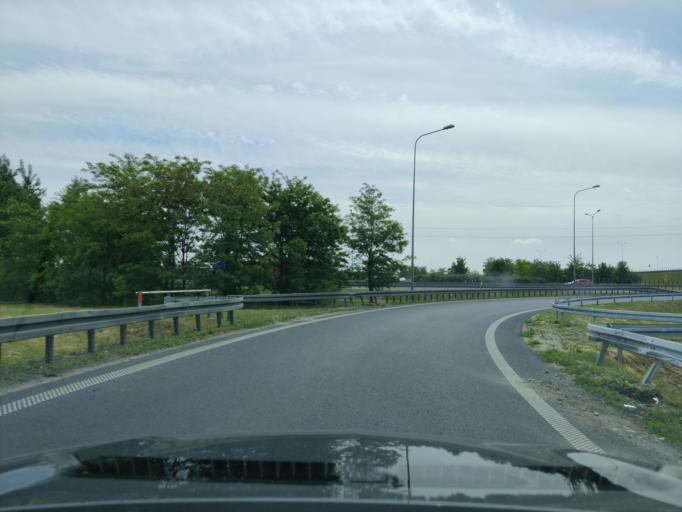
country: PL
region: Greater Poland Voivodeship
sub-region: Powiat poznanski
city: Komorniki
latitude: 52.3473
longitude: 16.7552
